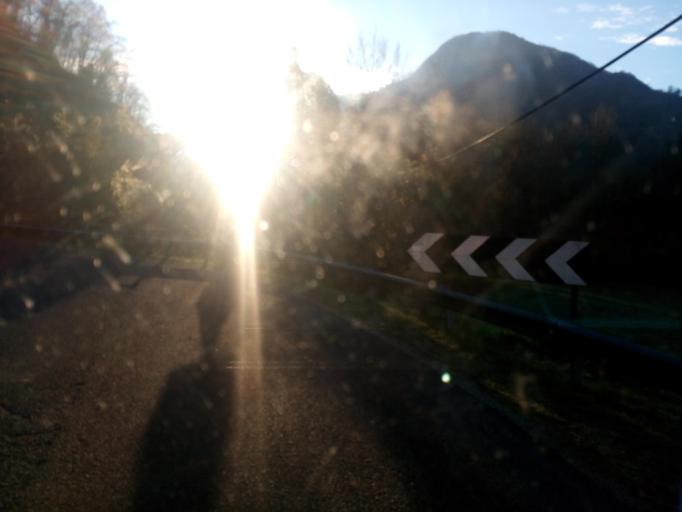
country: IT
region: Veneto
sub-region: Provincia di Vicenza
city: Valli del Pasubio
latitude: 45.7232
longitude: 11.2817
